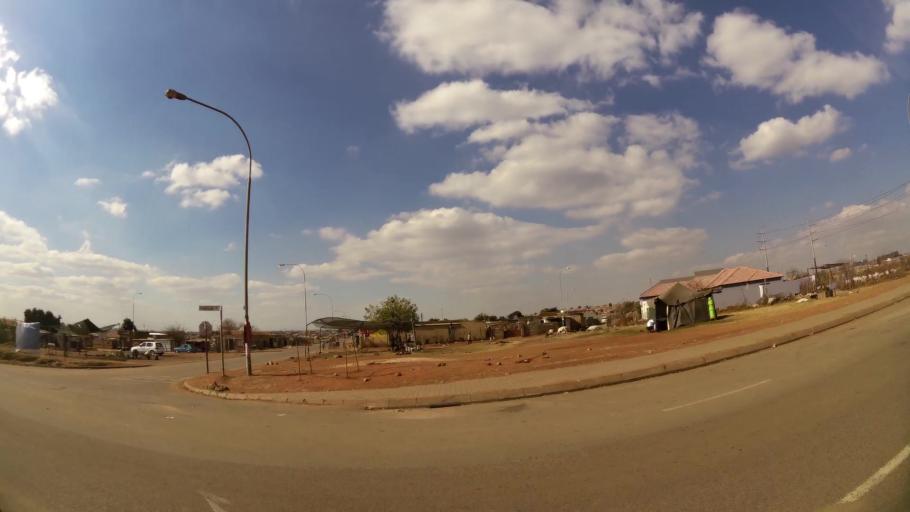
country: ZA
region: Gauteng
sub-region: Ekurhuleni Metropolitan Municipality
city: Tembisa
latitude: -25.9886
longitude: 28.2136
